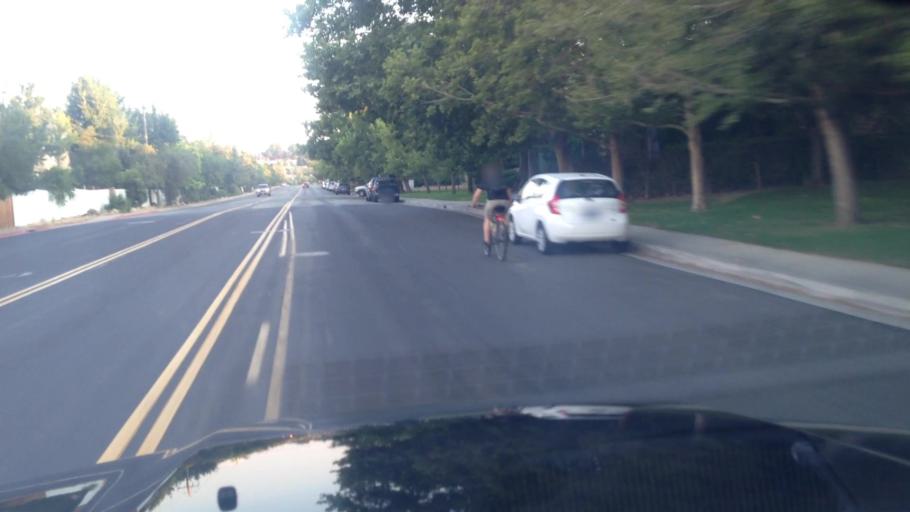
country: US
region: Nevada
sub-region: Washoe County
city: Reno
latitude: 39.4758
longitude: -119.8080
